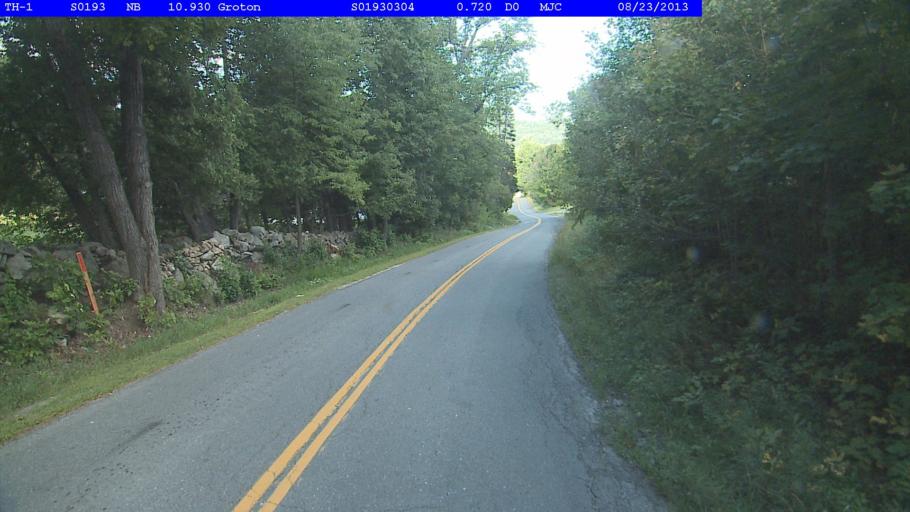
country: US
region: New Hampshire
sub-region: Grafton County
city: Woodsville
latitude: 44.1975
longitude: -72.2127
